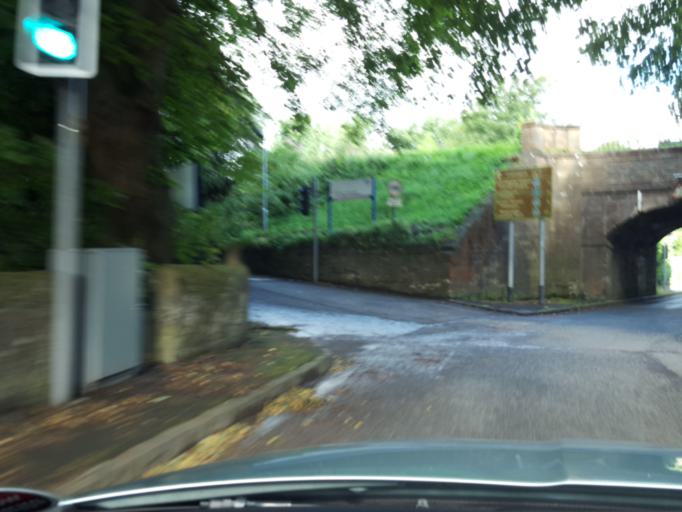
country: GB
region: Scotland
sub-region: West Lothian
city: Linlithgow
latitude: 55.9757
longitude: -3.5843
